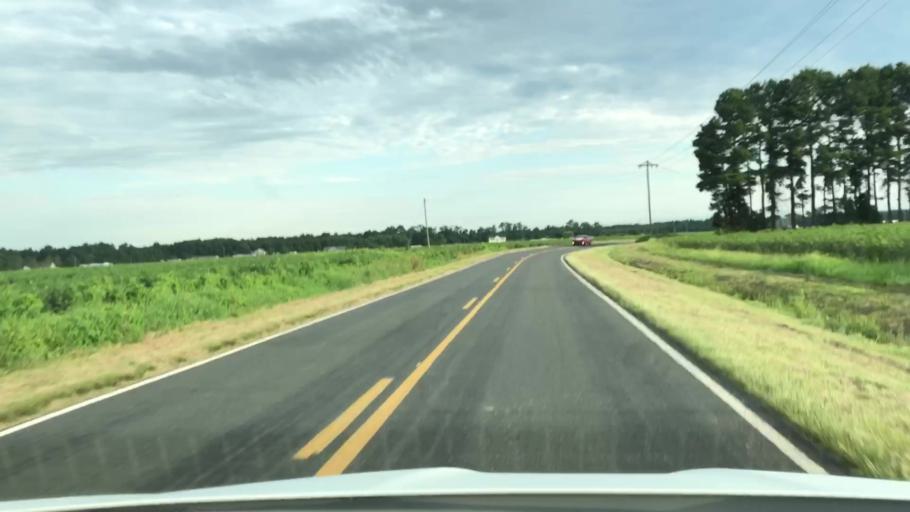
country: US
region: North Carolina
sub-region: Jones County
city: Maysville
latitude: 34.9896
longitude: -77.2802
